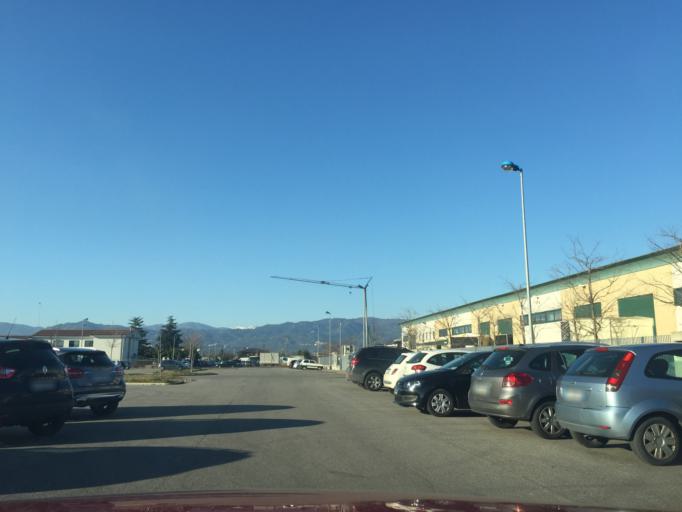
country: IT
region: Tuscany
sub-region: Provincia di Pistoia
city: Ponte Buggianese
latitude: 43.8440
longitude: 10.7629
